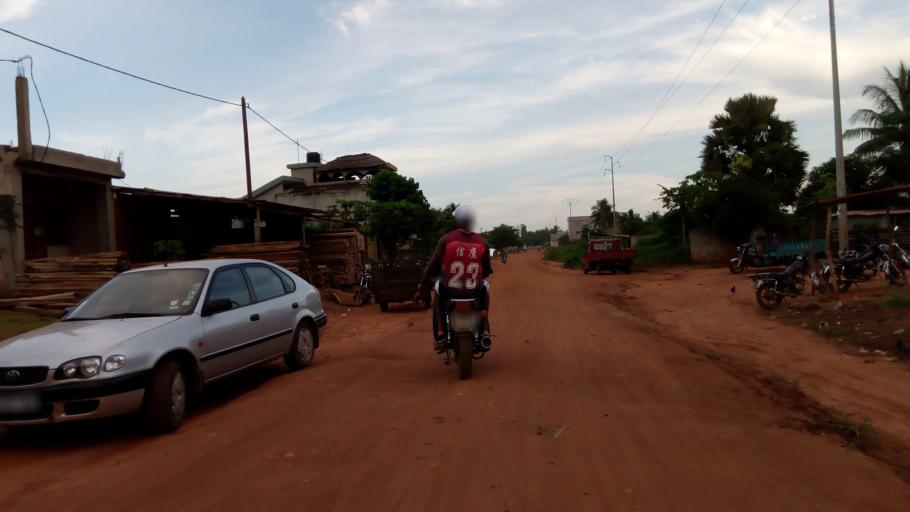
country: TG
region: Maritime
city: Lome
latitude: 6.2603
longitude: 1.1389
